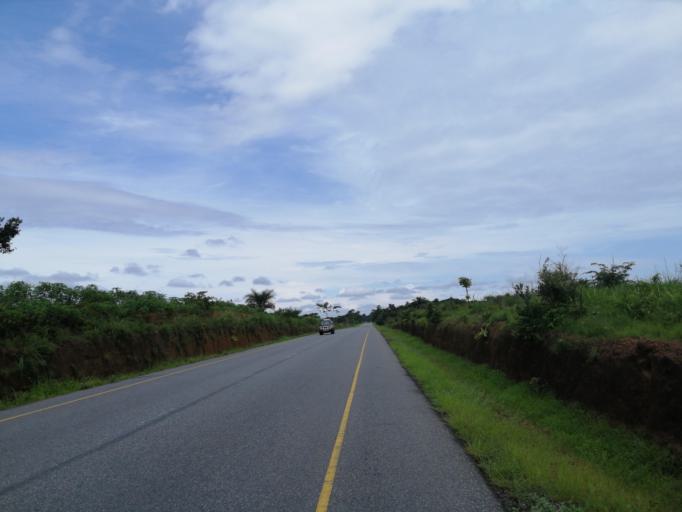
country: SL
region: Northern Province
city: Port Loko
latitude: 8.7455
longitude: -12.9255
